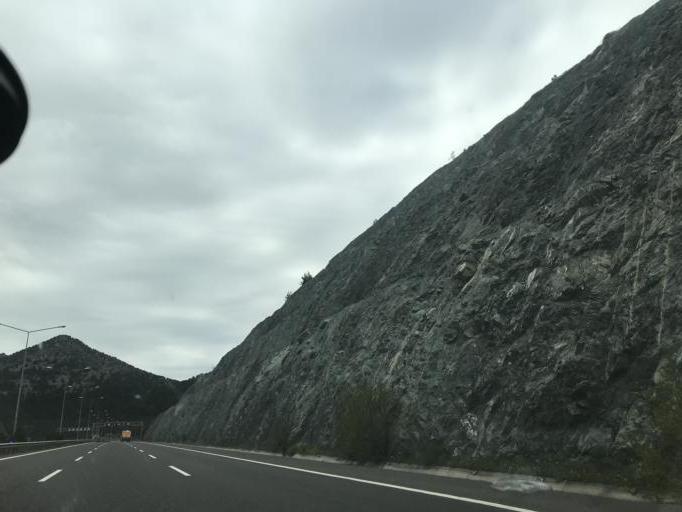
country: TR
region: Nigde
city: Ciftehan
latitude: 37.5004
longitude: 34.8260
